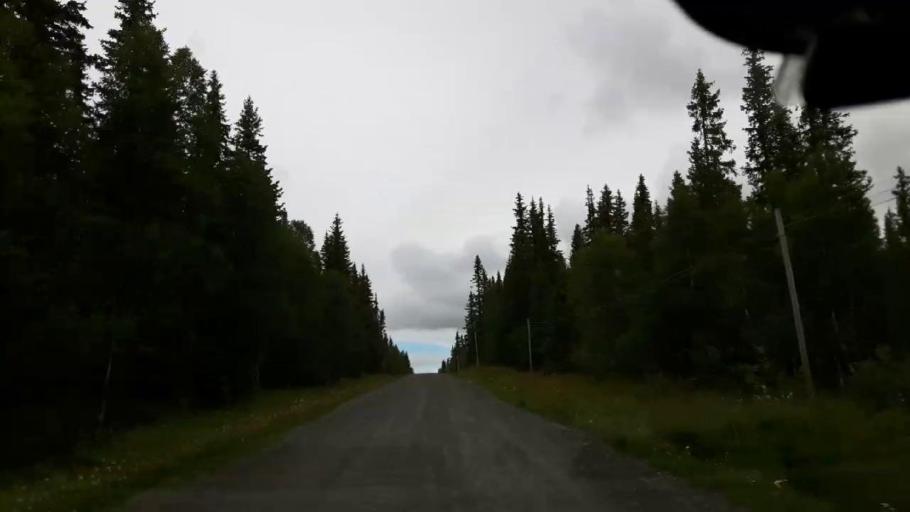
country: SE
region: Jaemtland
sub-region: Krokoms Kommun
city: Valla
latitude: 63.7399
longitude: 13.8377
